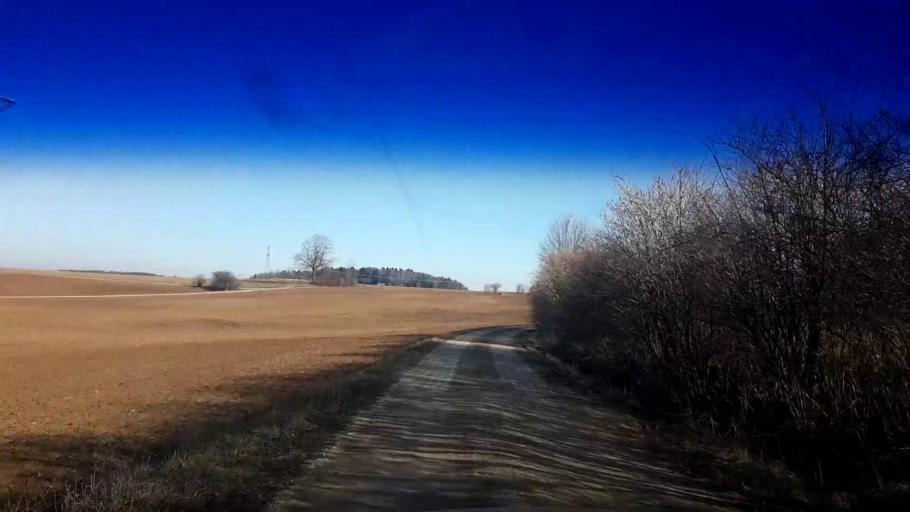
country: DE
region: Bavaria
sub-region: Upper Franconia
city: Poxdorf
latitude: 49.9662
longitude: 11.0927
